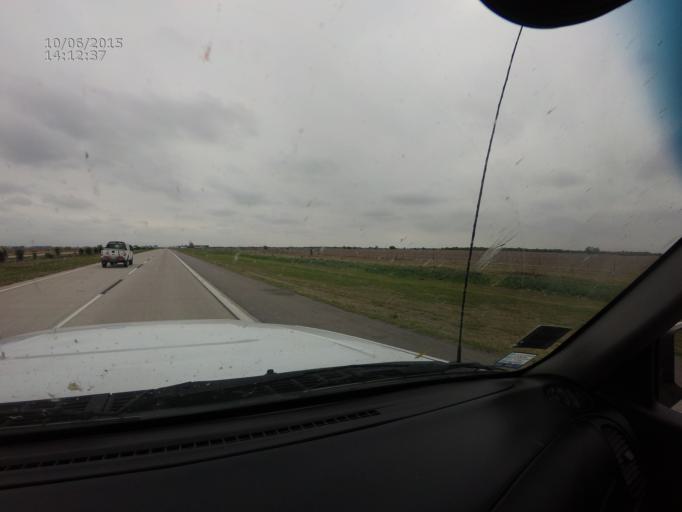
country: AR
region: Cordoba
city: Villa Maria
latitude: -32.4376
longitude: -63.1239
